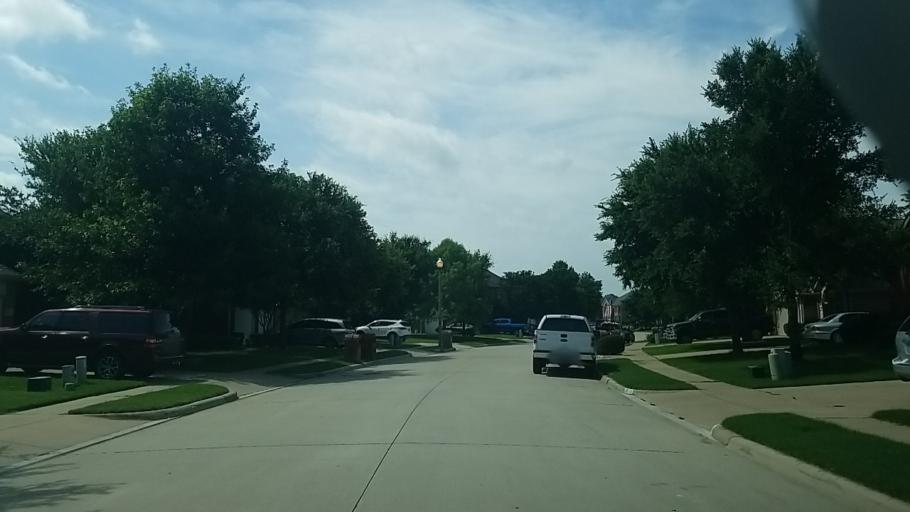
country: US
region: Texas
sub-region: Denton County
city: Corinth
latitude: 33.1505
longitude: -97.0965
